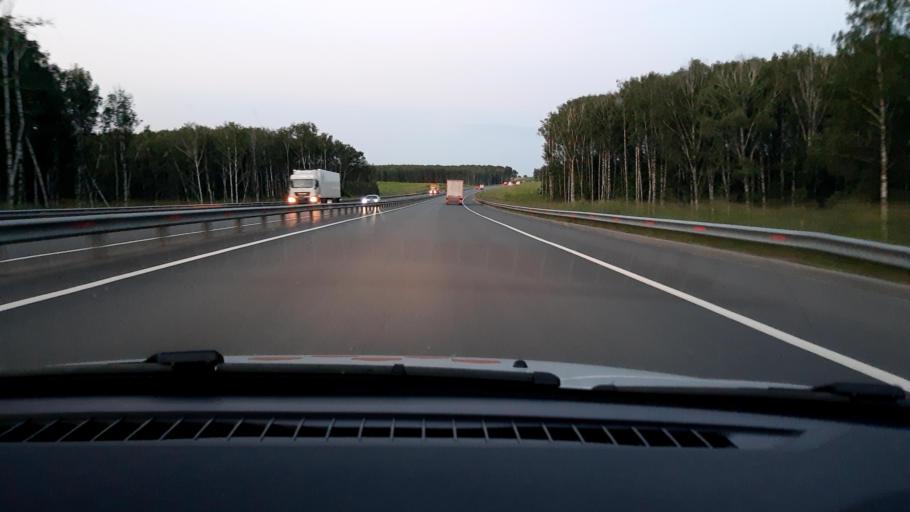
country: RU
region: Nizjnij Novgorod
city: Kstovo
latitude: 56.0999
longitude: 44.0539
